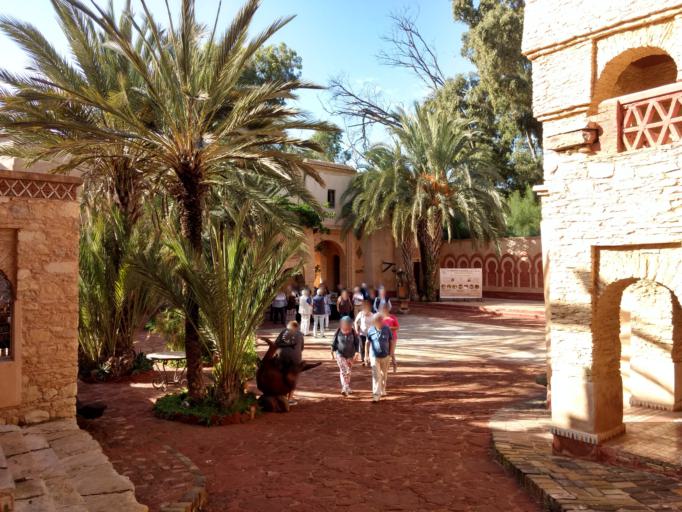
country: MA
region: Oued ed Dahab-Lagouira
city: Dakhla
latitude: 30.3786
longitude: -9.5722
